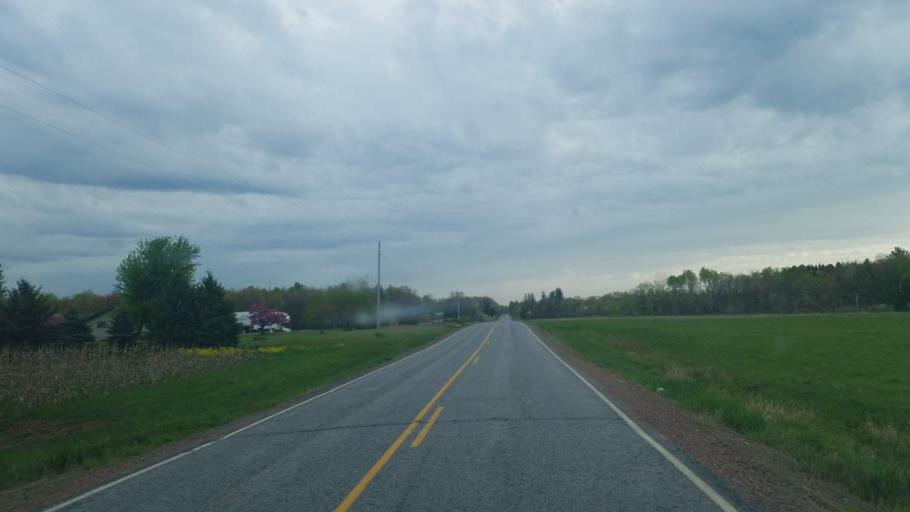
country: US
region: Wisconsin
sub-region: Wood County
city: Nekoosa
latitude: 44.3949
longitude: -90.1602
